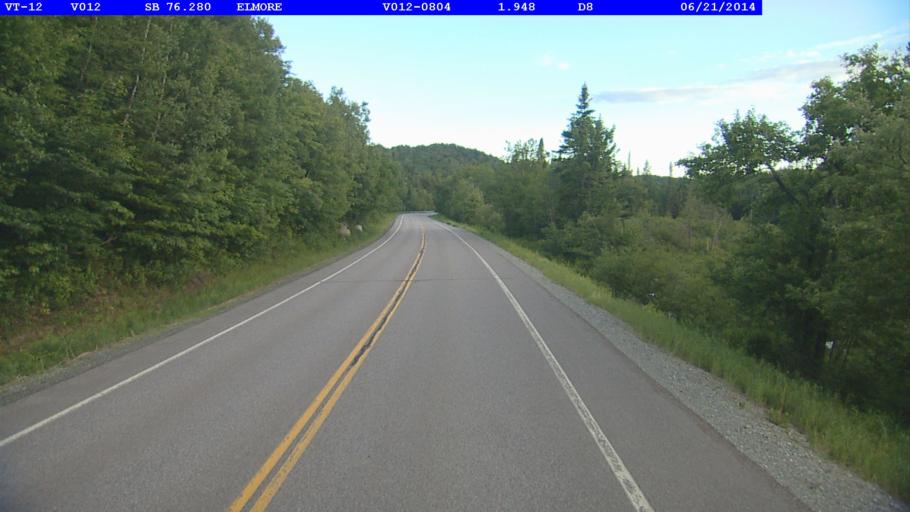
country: US
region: Vermont
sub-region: Lamoille County
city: Morrisville
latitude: 44.4752
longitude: -72.5306
